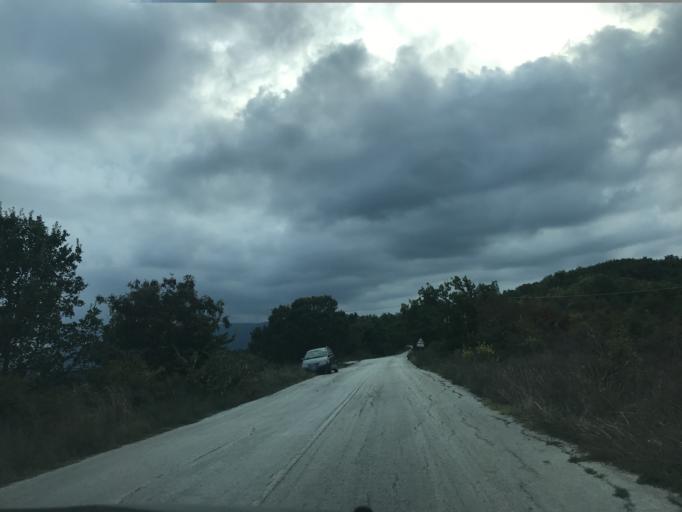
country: IT
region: Molise
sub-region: Provincia di Isernia
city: Bagnoli del Trigno
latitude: 41.6856
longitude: 14.4591
